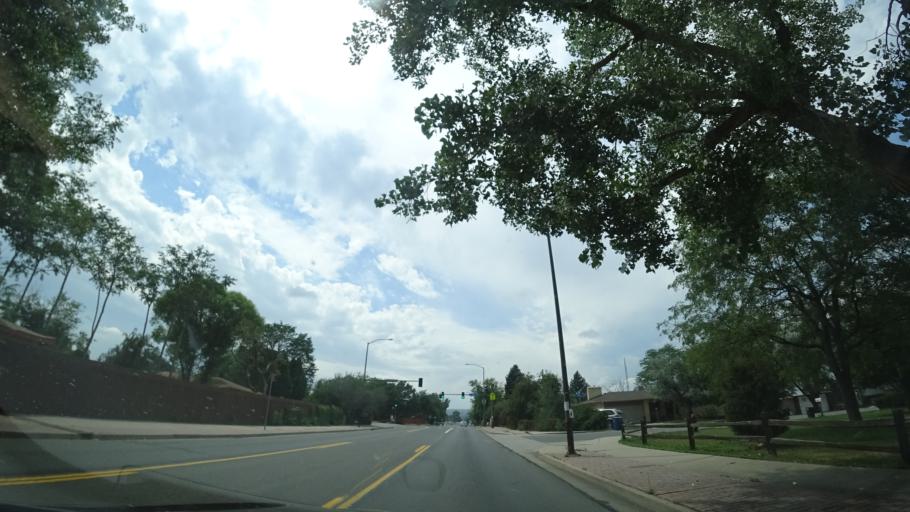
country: US
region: Colorado
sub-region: Jefferson County
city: Lakewood
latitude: 39.6966
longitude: -105.0770
